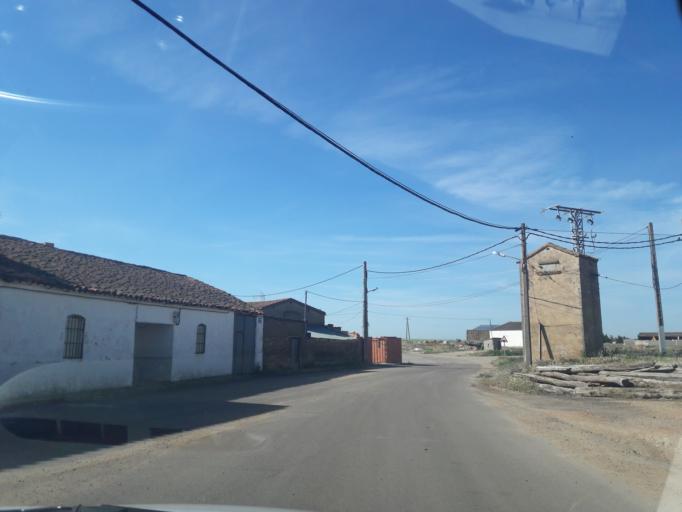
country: ES
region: Castille and Leon
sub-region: Provincia de Salamanca
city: Parada de Rubiales
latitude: 41.1466
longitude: -5.4380
